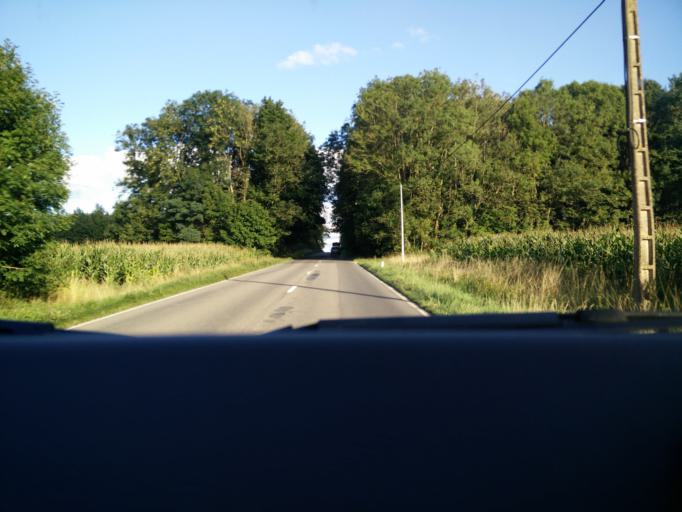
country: BE
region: Wallonia
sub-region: Province de Namur
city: Philippeville
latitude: 50.2034
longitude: 4.4873
